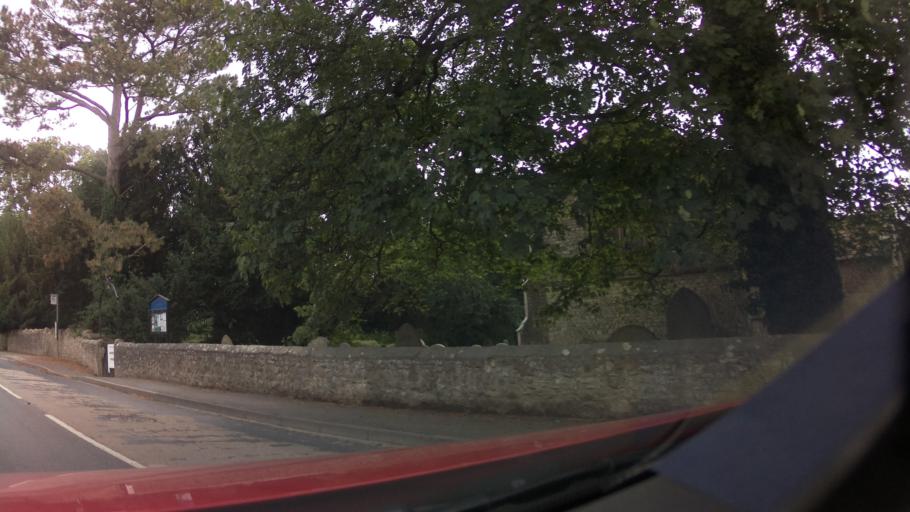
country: GB
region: England
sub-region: North Yorkshire
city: Ripon
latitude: 54.1885
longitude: -1.5626
